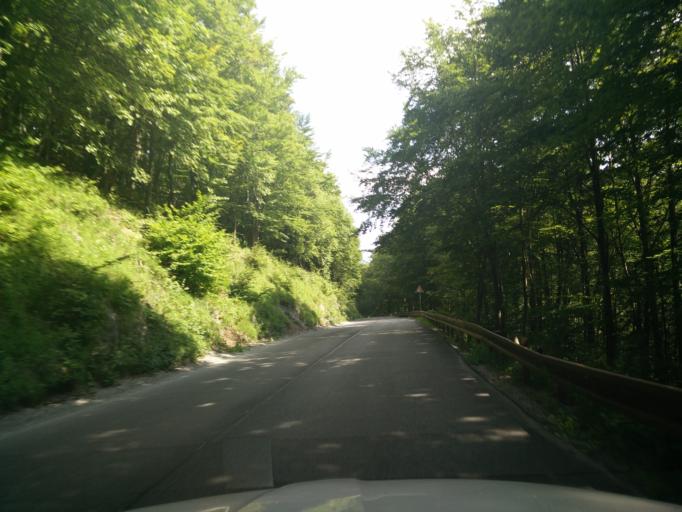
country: SK
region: Zilinsky
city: Rajec
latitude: 48.9550
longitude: 18.6186
